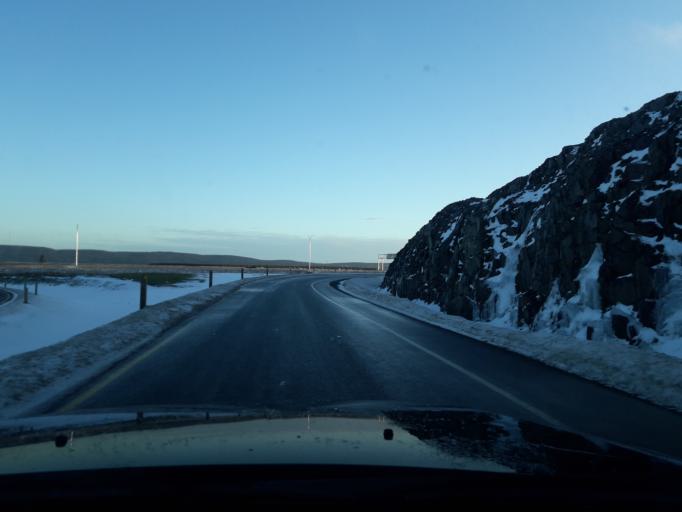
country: CA
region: Newfoundland and Labrador
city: Mount Pearl
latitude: 47.5477
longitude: -52.7661
